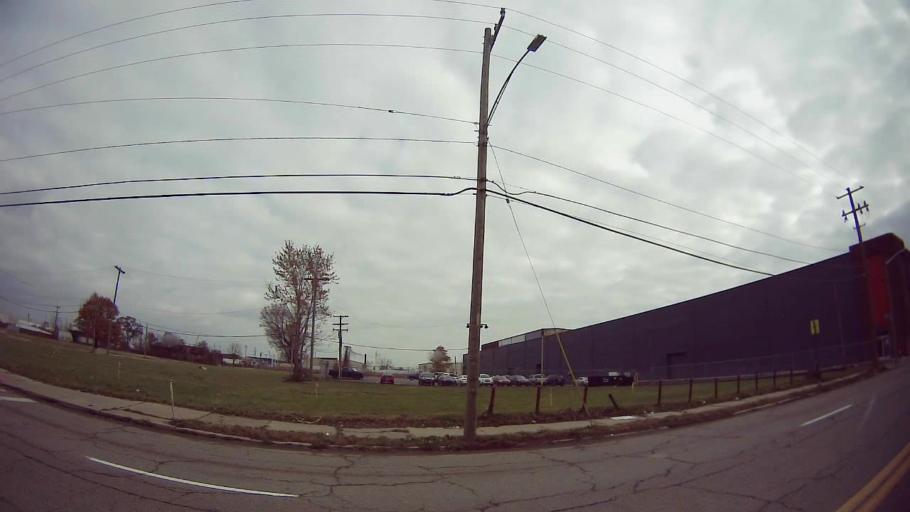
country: US
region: Michigan
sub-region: Wayne County
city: Hamtramck
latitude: 42.3930
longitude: -83.0374
